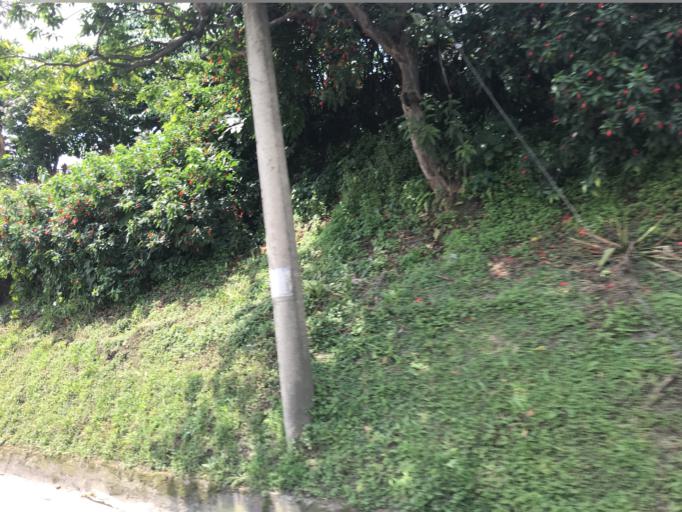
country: CO
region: Quindio
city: Calarca
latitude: 4.5231
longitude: -75.6420
